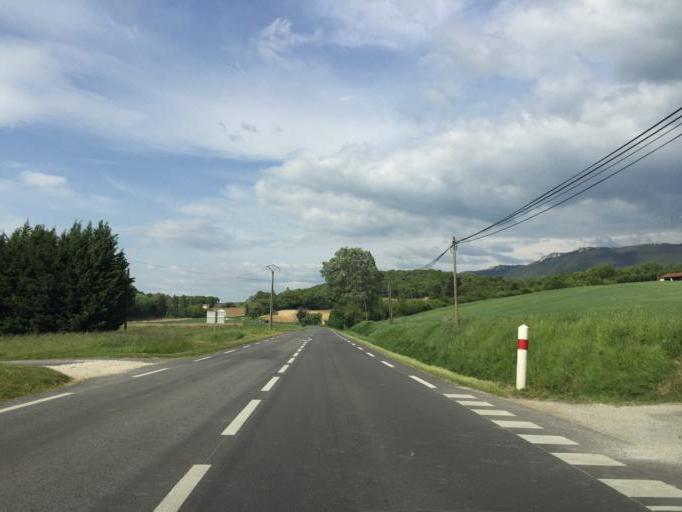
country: FR
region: Rhone-Alpes
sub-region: Departement de la Drome
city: Eurre
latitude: 44.7809
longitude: 5.0228
